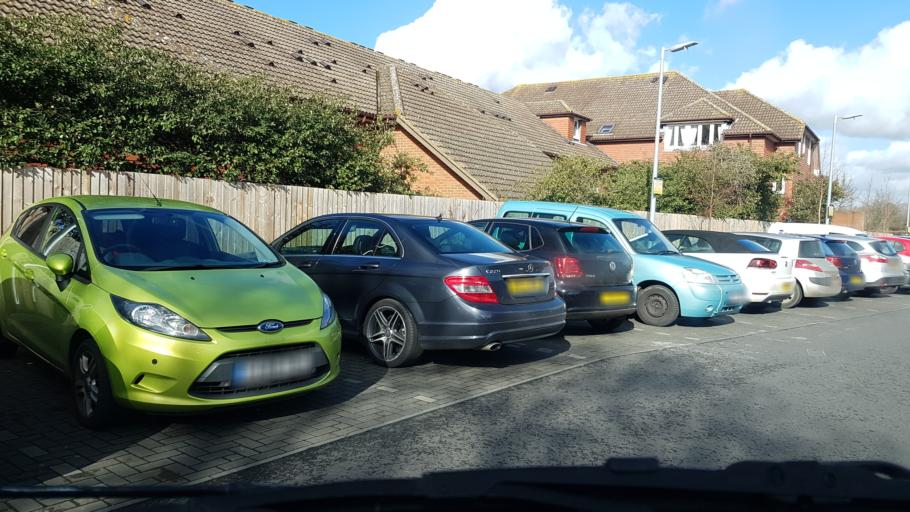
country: GB
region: England
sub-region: Surrey
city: Send
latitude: 51.2585
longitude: -0.5461
